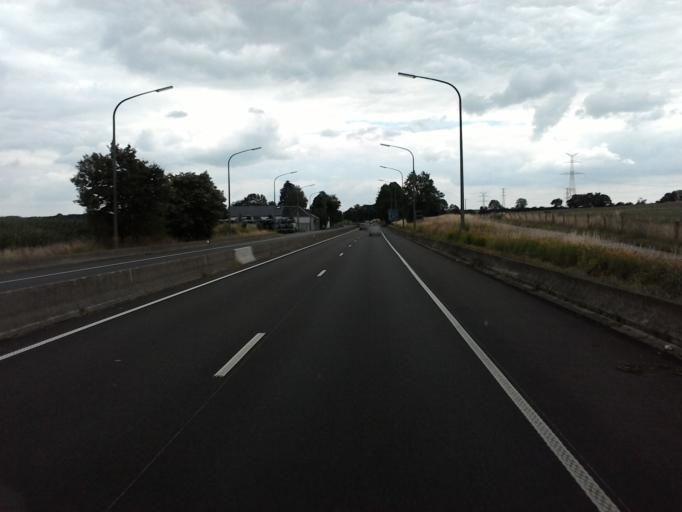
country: BE
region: Wallonia
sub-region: Province du Luxembourg
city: Martelange
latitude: 49.8698
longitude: 5.7114
